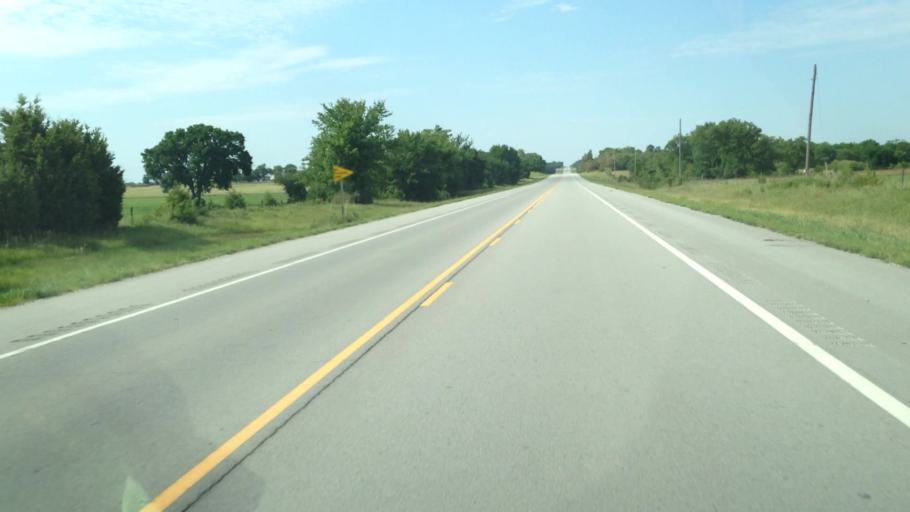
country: US
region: Kansas
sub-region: Labette County
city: Parsons
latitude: 37.2837
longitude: -95.2675
